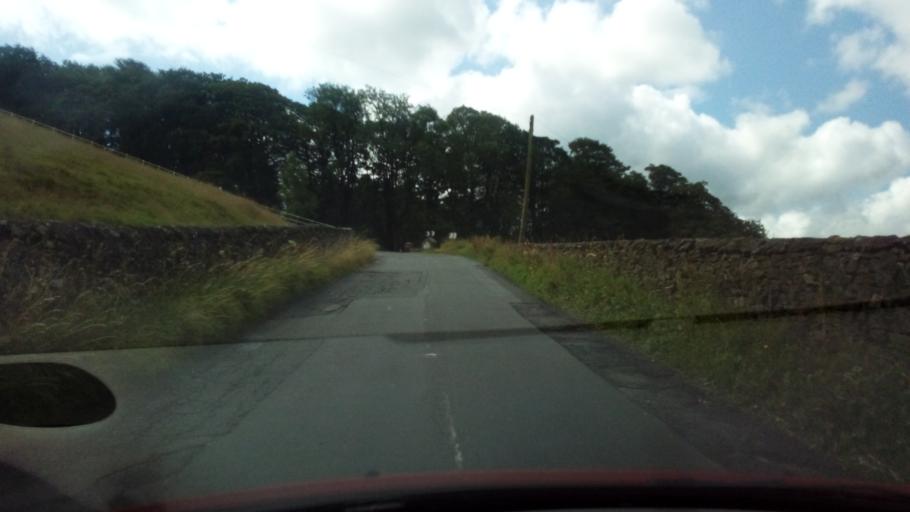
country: GB
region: England
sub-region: Lancashire
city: Clitheroe
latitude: 53.9649
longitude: -2.4359
